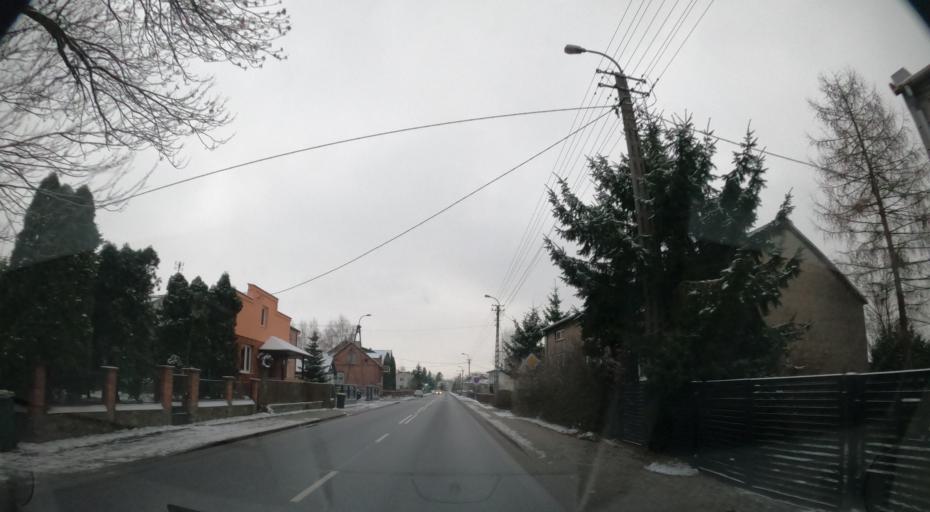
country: PL
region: Kujawsko-Pomorskie
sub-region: Powiat lipnowski
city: Wielgie
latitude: 52.7399
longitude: 19.2689
